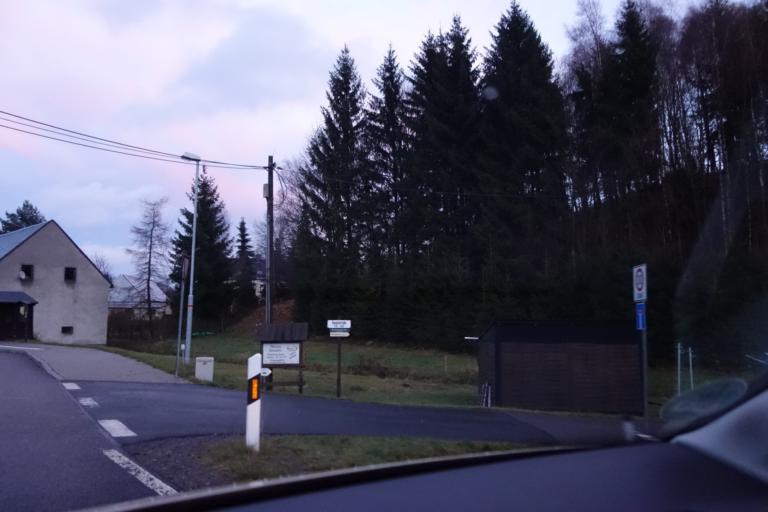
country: DE
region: Saxony
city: Neuhausen
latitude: 50.7042
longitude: 13.4912
